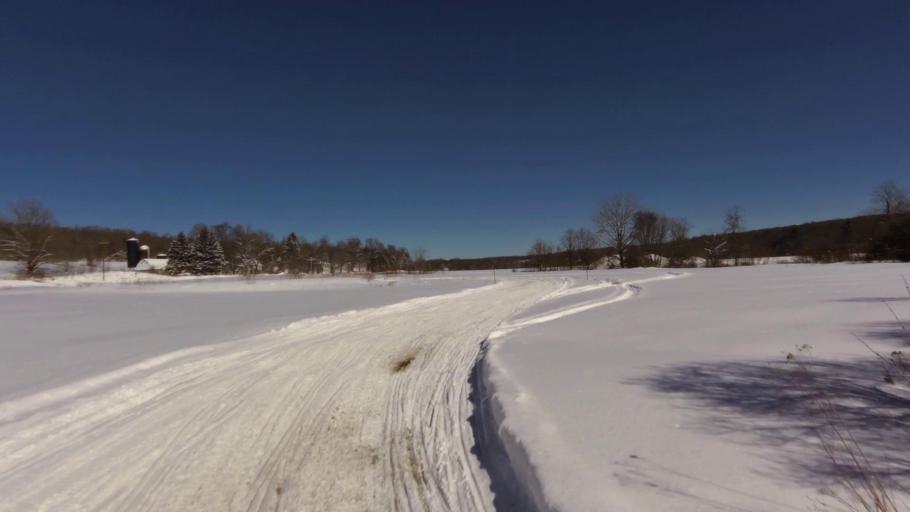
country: US
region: New York
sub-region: Chautauqua County
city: Mayville
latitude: 42.2501
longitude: -79.4404
